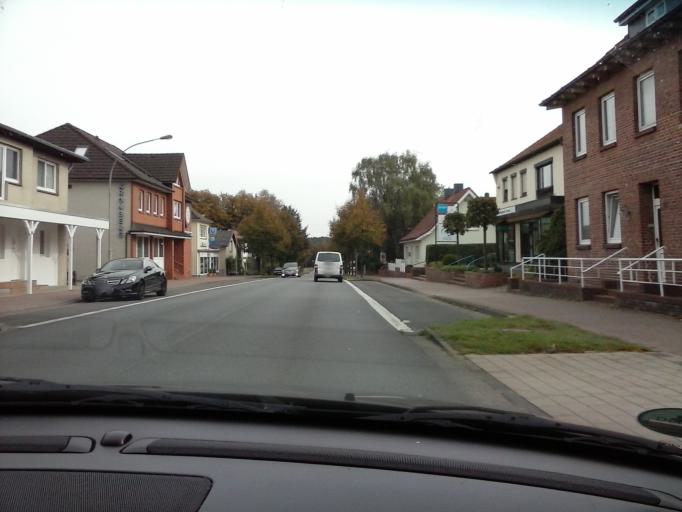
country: DE
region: Lower Saxony
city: Hemmoor
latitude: 53.7001
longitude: 9.1398
